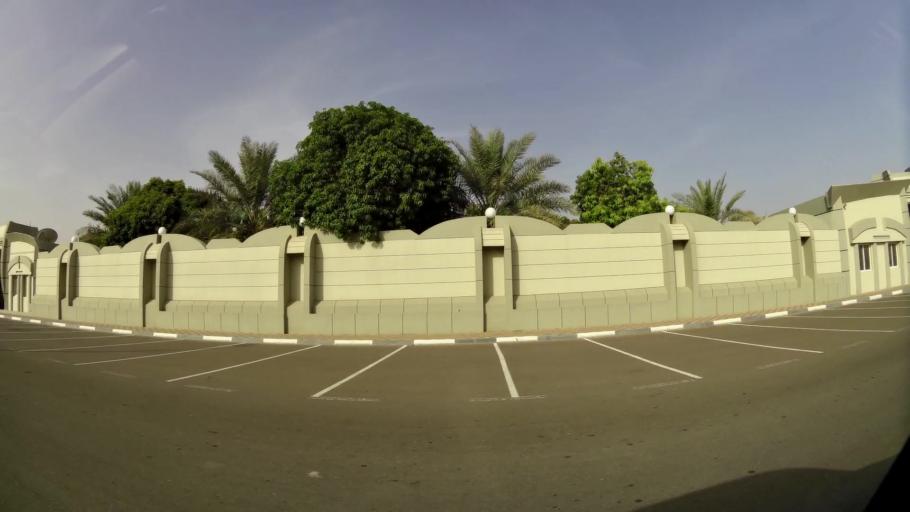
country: AE
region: Abu Dhabi
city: Al Ain
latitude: 24.1257
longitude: 55.6818
